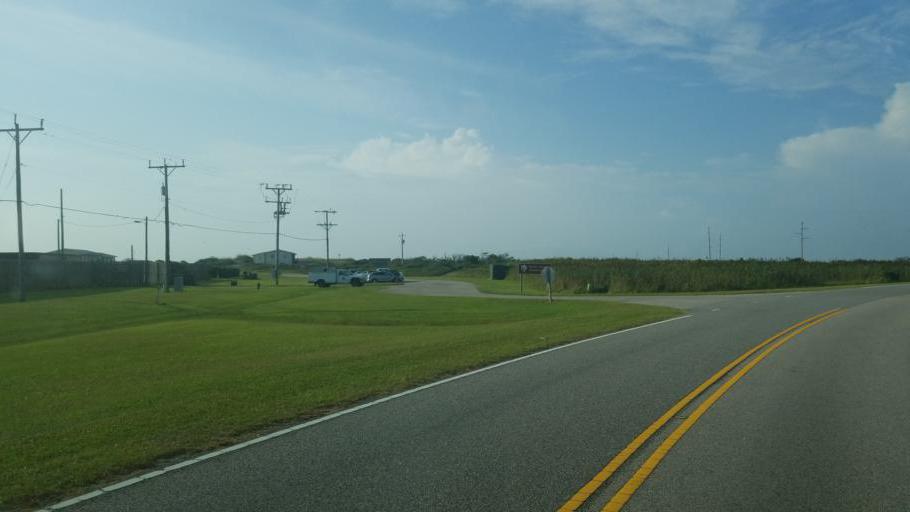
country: US
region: North Carolina
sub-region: Dare County
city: Wanchese
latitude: 35.8461
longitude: -75.5649
